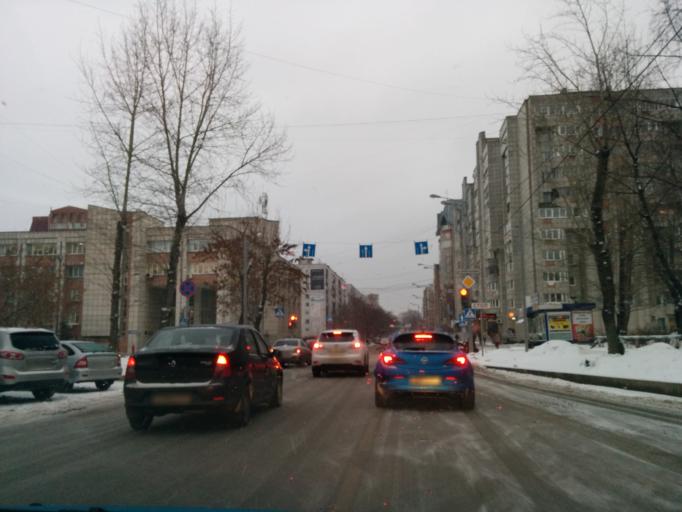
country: RU
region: Perm
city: Perm
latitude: 58.0026
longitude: 56.2142
